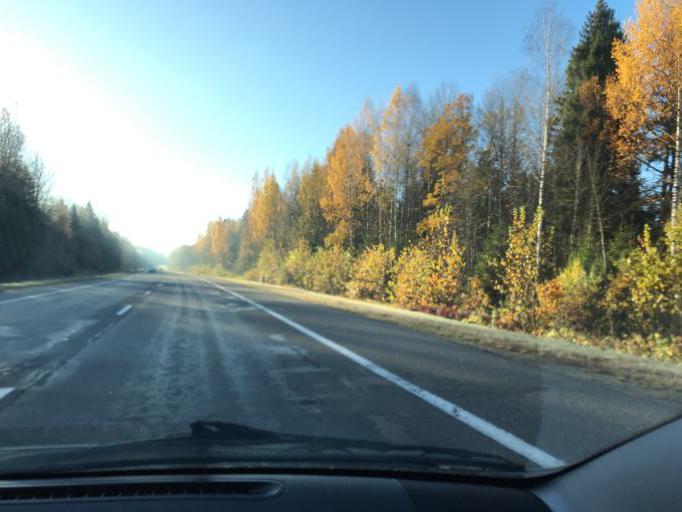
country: BY
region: Vitebsk
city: Vitebsk
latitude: 54.8968
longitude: 30.3784
